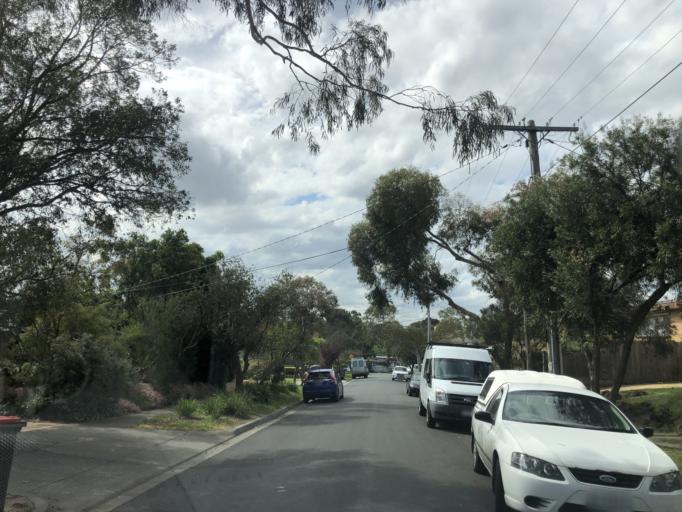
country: AU
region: Victoria
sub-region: Monash
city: Ashwood
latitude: -37.8621
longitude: 145.1066
